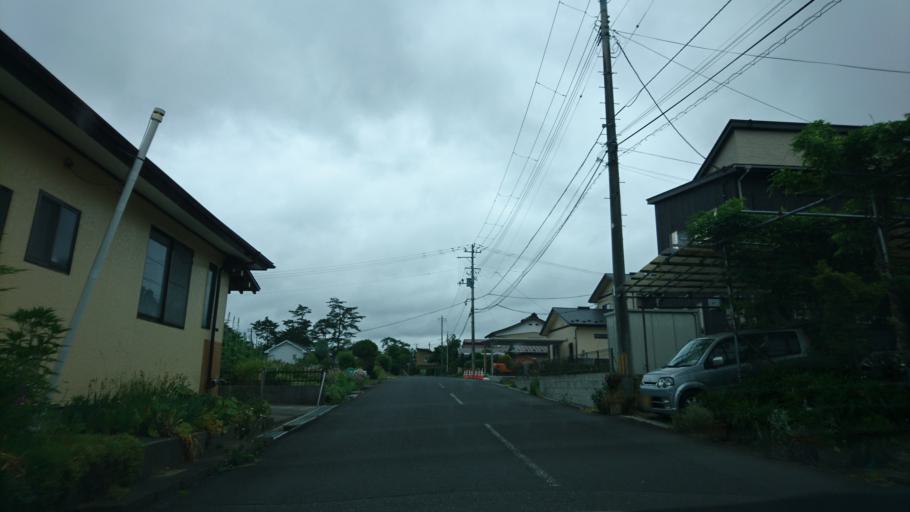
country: JP
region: Iwate
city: Ichinoseki
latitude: 38.9115
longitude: 141.1687
